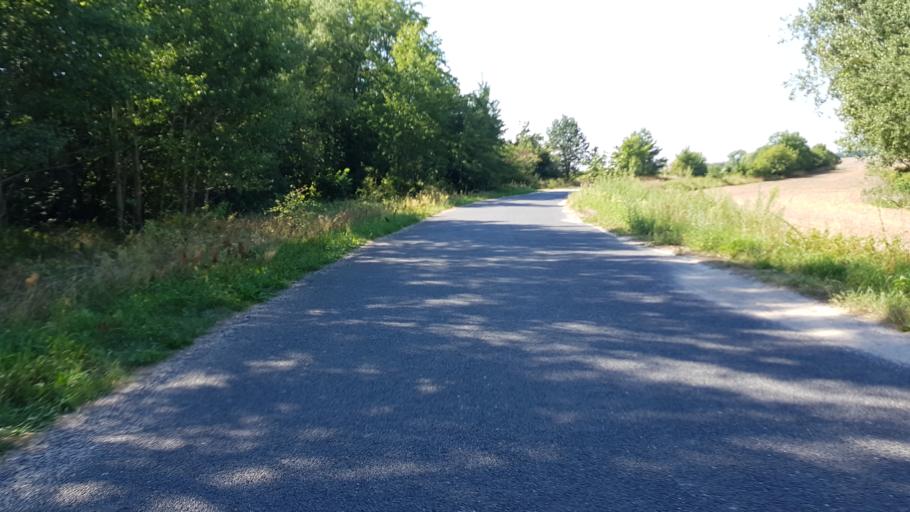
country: PL
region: West Pomeranian Voivodeship
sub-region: Powiat gryfinski
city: Gryfino
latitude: 53.1572
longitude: 14.4945
